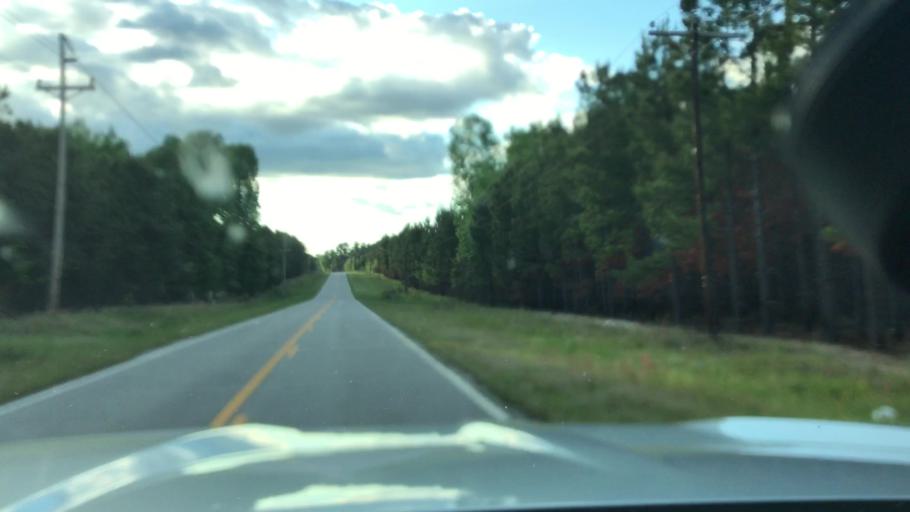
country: US
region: South Carolina
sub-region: Bamberg County
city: Denmark
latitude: 33.4707
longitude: -81.1688
